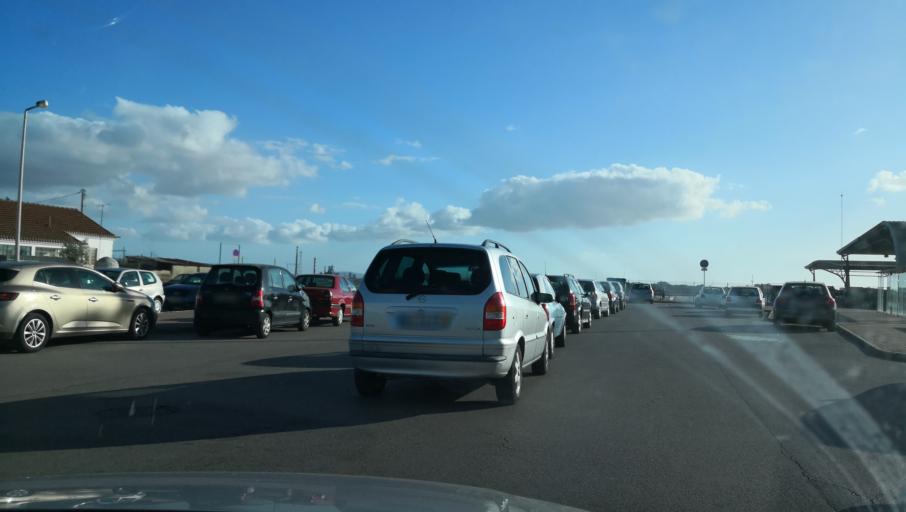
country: PT
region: Setubal
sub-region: Barreiro
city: Barreiro
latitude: 38.6523
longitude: -9.0770
